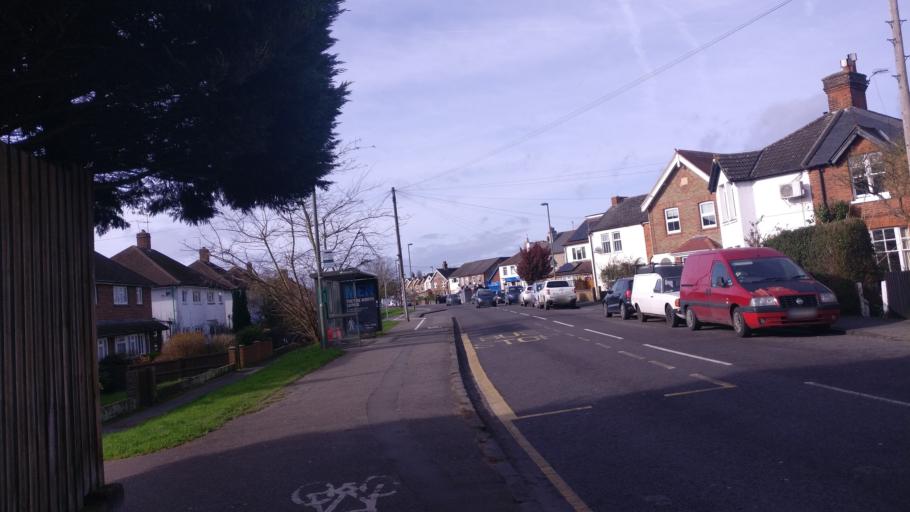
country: GB
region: England
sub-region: Surrey
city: Staines
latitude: 51.4277
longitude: -0.5245
